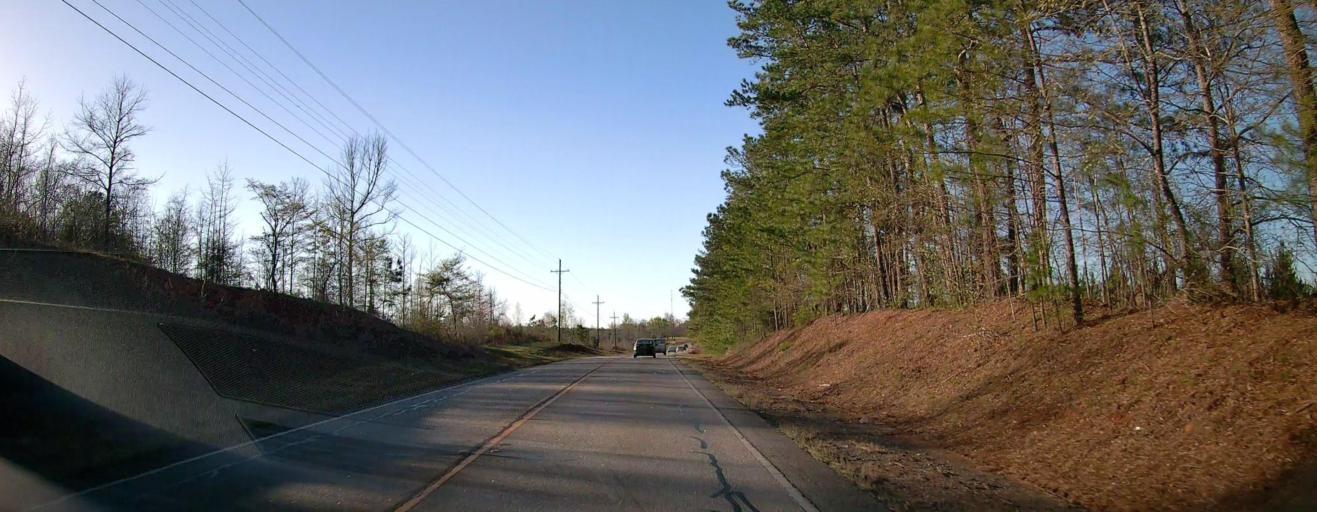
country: US
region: Georgia
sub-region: Butts County
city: Jackson
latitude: 33.4126
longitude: -83.8926
